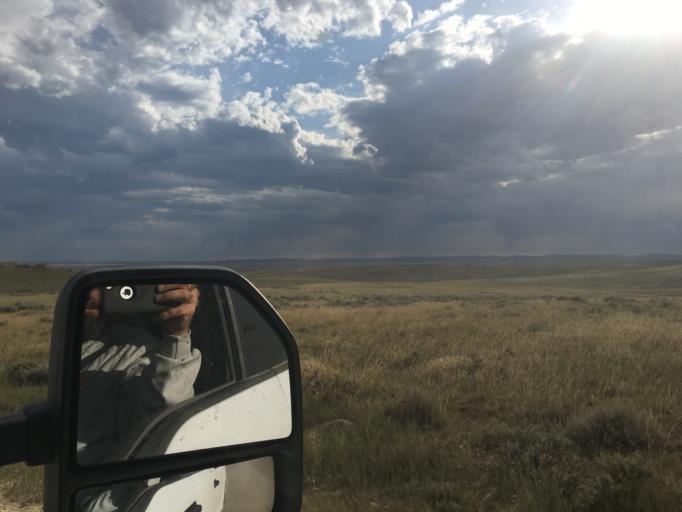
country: US
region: Wyoming
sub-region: Campbell County
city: Wright
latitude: 43.4951
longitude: -105.8593
